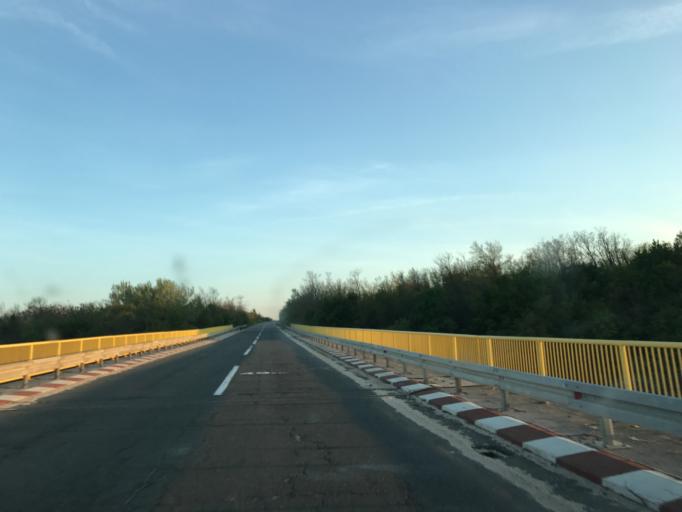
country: RO
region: Mehedinti
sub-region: Comuna Gogosu
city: Ostrovu Mare
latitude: 44.3693
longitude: 22.4801
